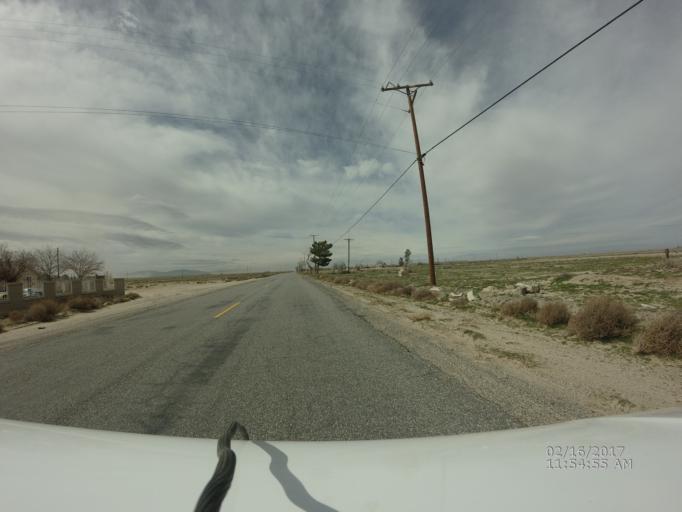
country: US
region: California
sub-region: Los Angeles County
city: Lake Los Angeles
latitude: 34.6900
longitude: -117.8941
